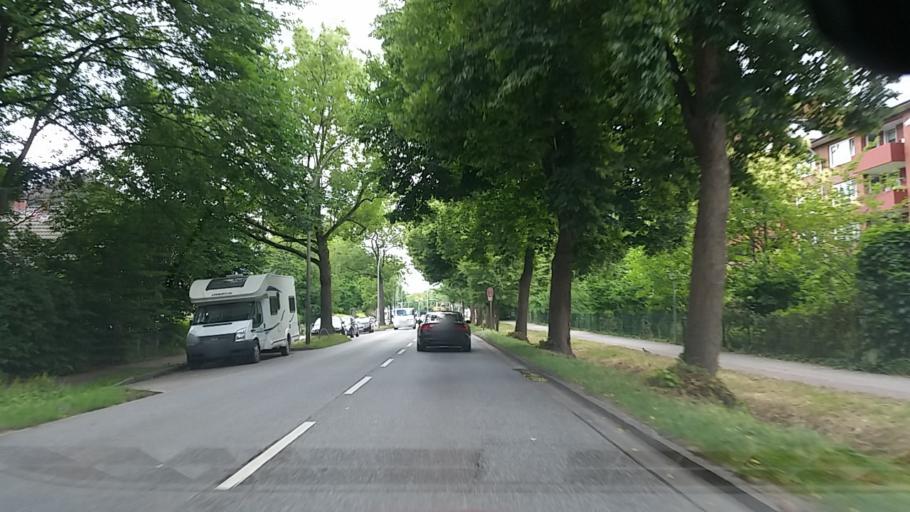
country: DE
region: Hamburg
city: Eidelstedt
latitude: 53.6306
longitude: 9.9105
